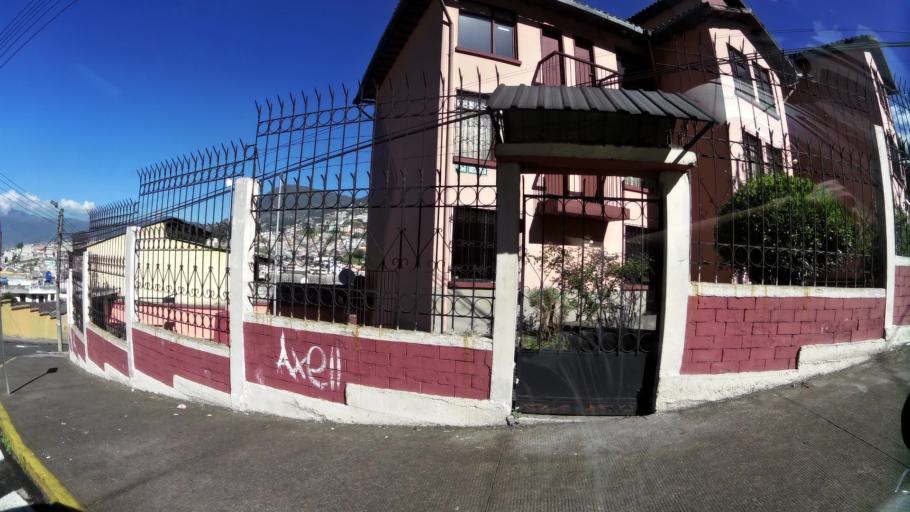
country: EC
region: Pichincha
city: Quito
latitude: -0.2290
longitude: -78.5221
